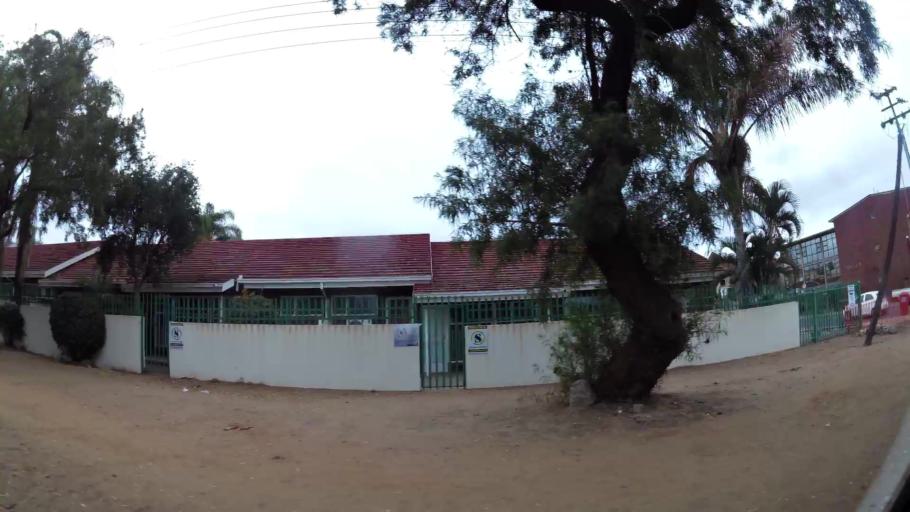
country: ZA
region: Limpopo
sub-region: Capricorn District Municipality
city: Polokwane
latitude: -23.9044
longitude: 29.4536
